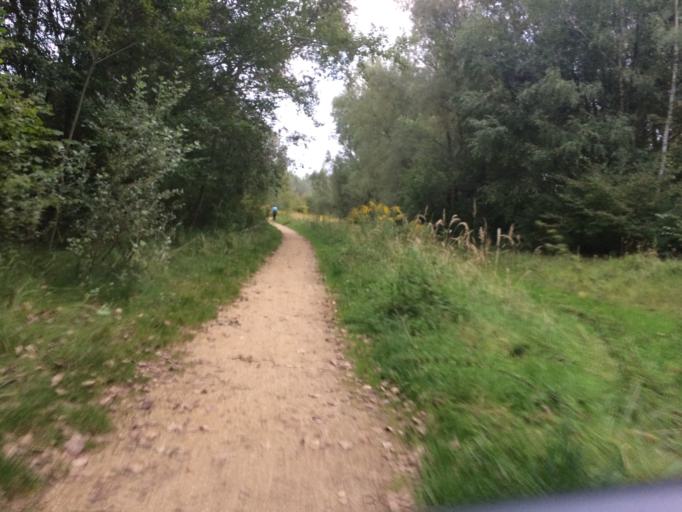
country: DE
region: Berlin
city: Heinersdorf
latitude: 52.5713
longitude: 13.4505
